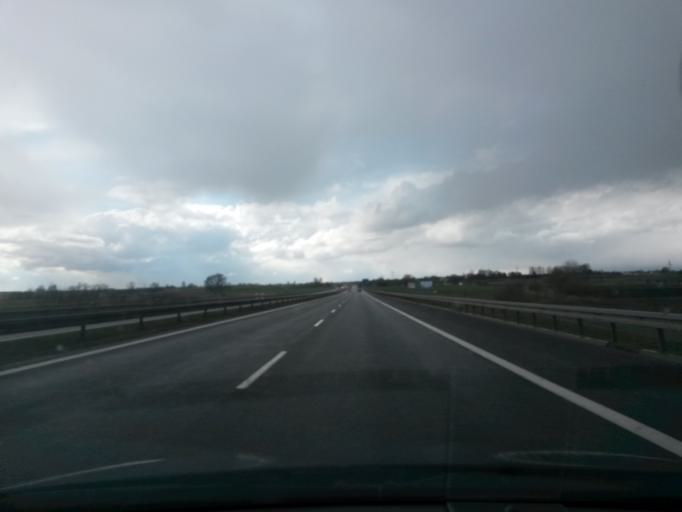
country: PL
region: Greater Poland Voivodeship
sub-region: Powiat poznanski
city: Swarzedz
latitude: 52.3392
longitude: 17.0436
